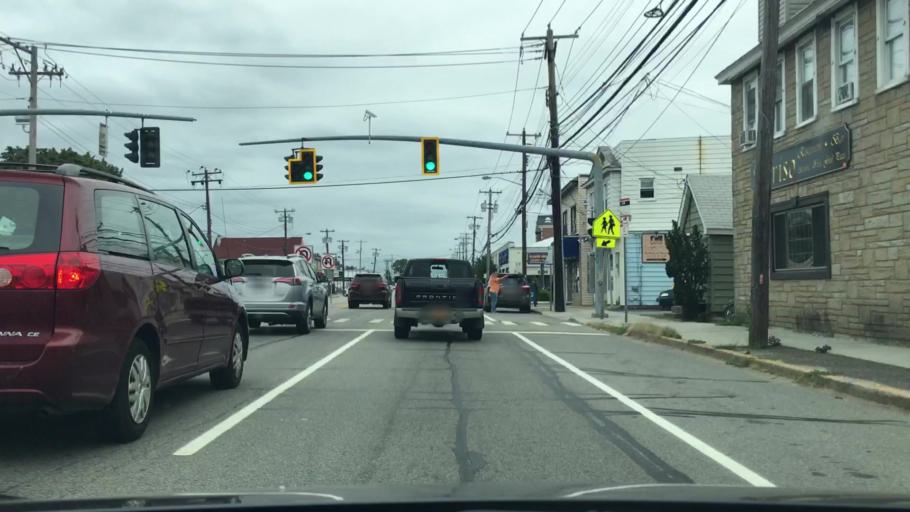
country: US
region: New York
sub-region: Nassau County
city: Garden City Park
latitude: 40.7392
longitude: -73.6666
